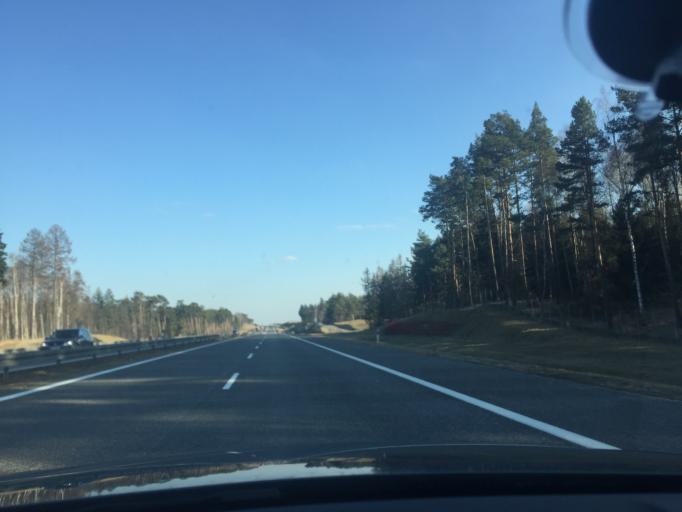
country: PL
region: Lubusz
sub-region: Powiat miedzyrzecki
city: Brojce
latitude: 52.3093
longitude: 15.6191
